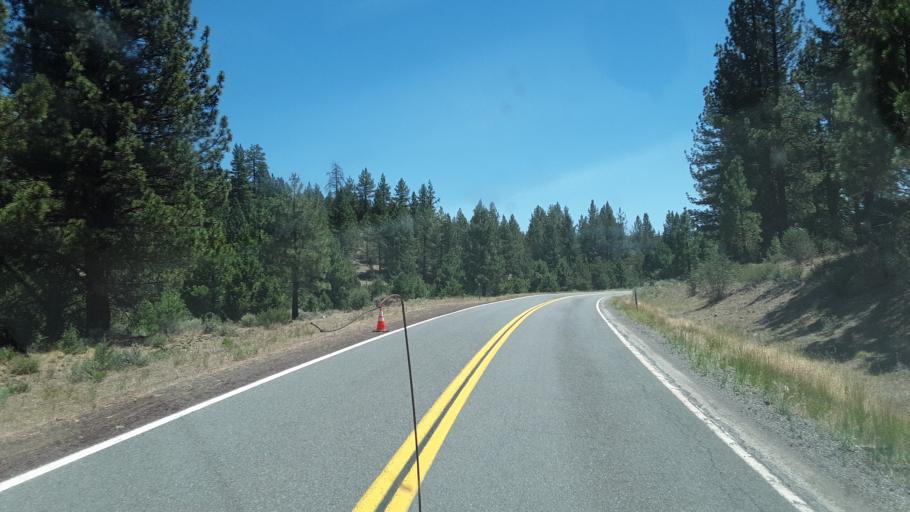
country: US
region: California
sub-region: Modoc County
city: Alturas
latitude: 41.0005
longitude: -120.8096
